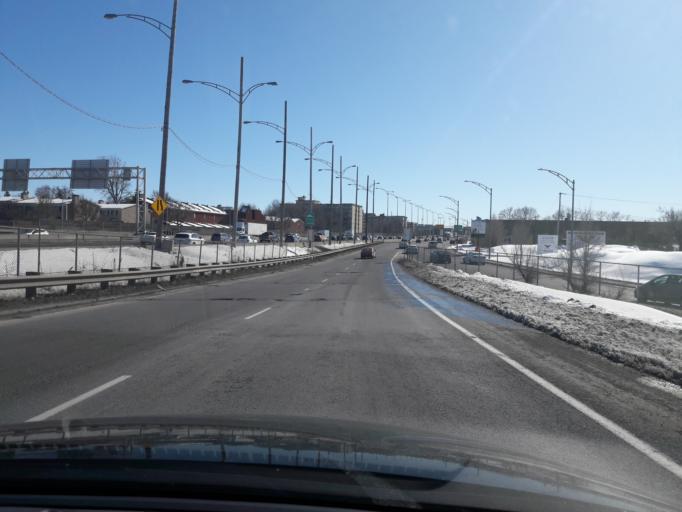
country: CA
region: Quebec
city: Mont-Royal
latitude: 45.5253
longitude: -73.6526
